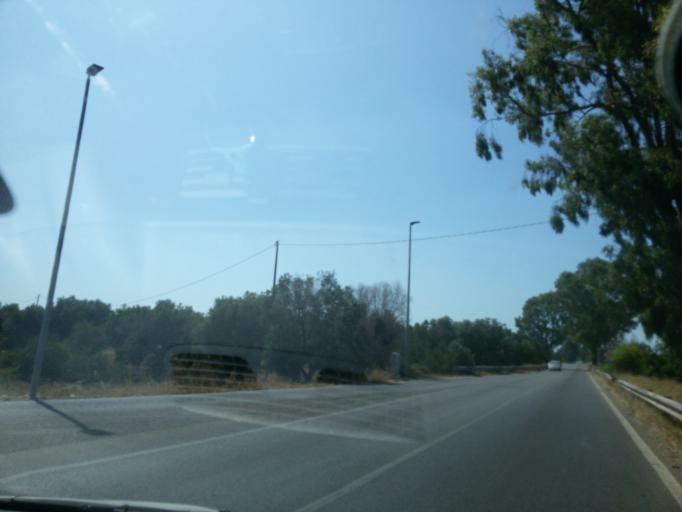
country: IT
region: Apulia
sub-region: Provincia di Lecce
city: Porto Cesareo
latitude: 40.2523
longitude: 17.9326
